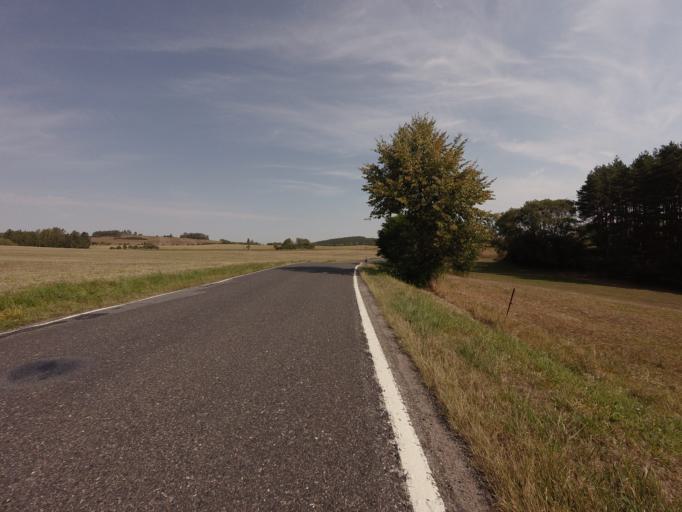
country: CZ
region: Central Bohemia
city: Petrovice
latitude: 49.5705
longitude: 14.3695
